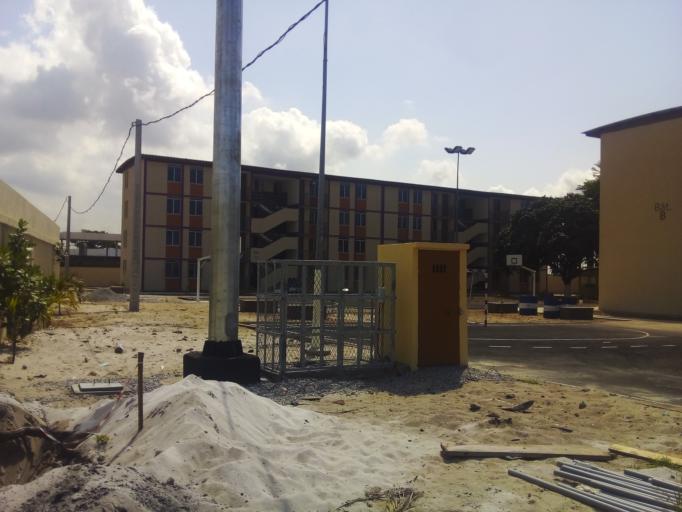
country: CI
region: Lagunes
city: Abidjan
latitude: 5.2626
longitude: -3.9610
